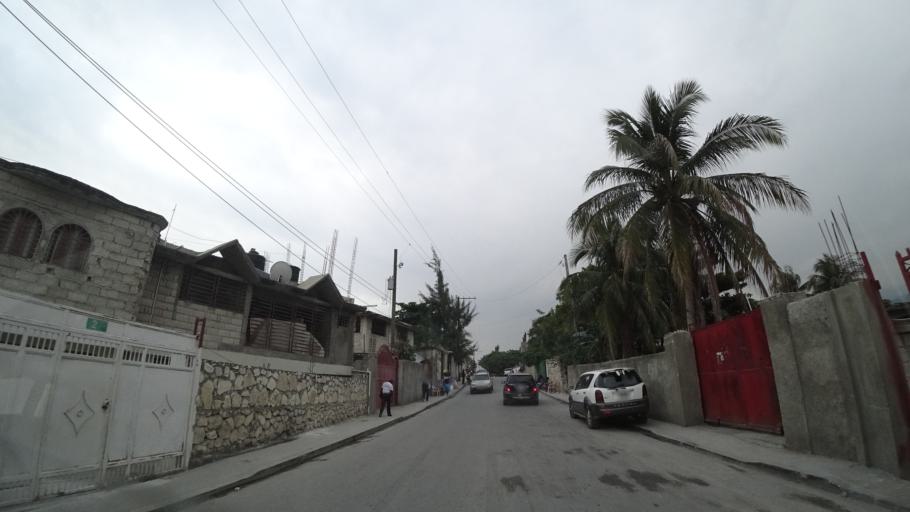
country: HT
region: Ouest
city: Delmas 73
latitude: 18.5627
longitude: -72.2950
